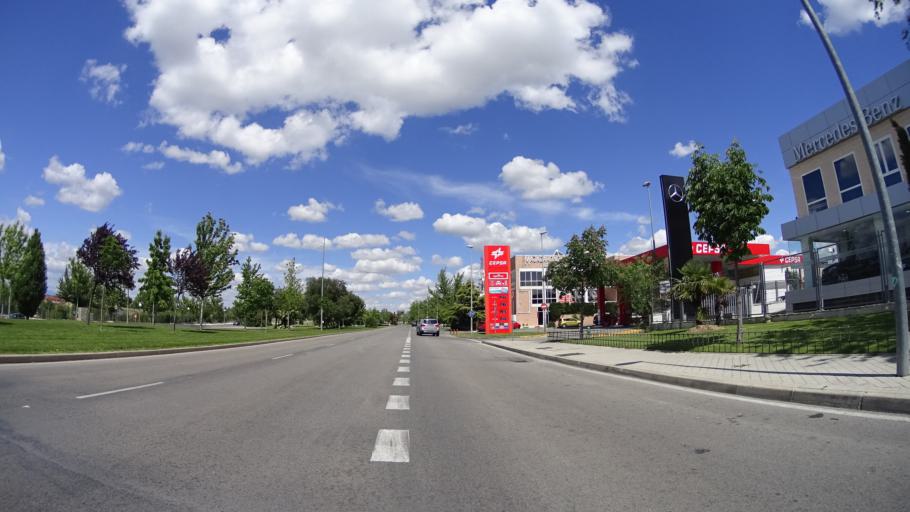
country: ES
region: Madrid
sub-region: Provincia de Madrid
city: Majadahonda
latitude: 40.4584
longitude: -3.8739
